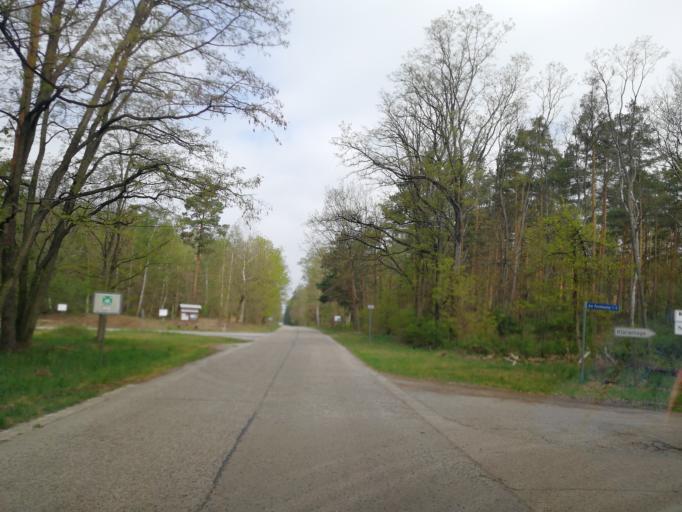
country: DE
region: Saxony
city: Beilrode
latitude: 51.6552
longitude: 13.1138
